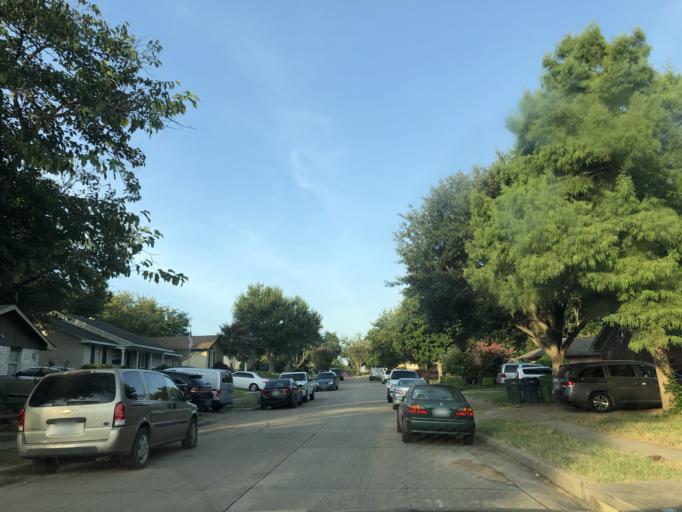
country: US
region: Texas
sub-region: Dallas County
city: Garland
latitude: 32.8628
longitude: -96.6274
